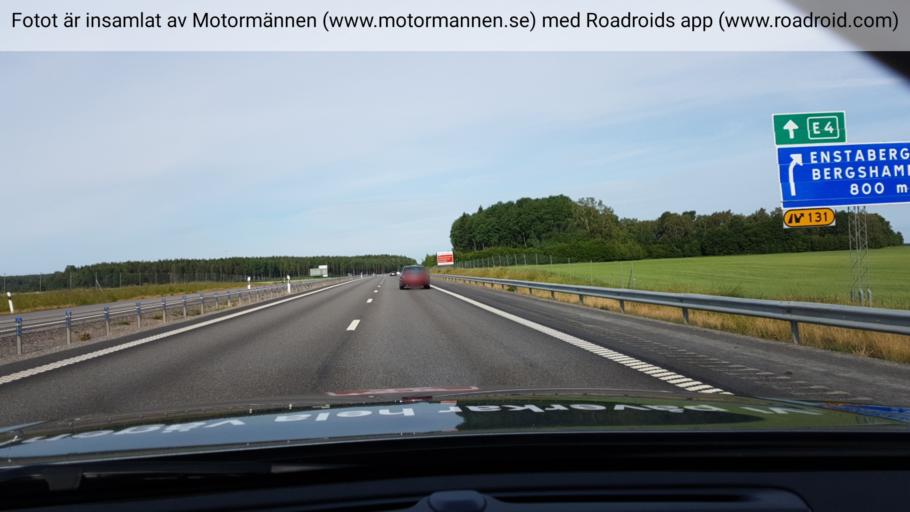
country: SE
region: Soedermanland
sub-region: Nykopings Kommun
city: Nykoping
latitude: 58.7474
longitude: 16.9560
